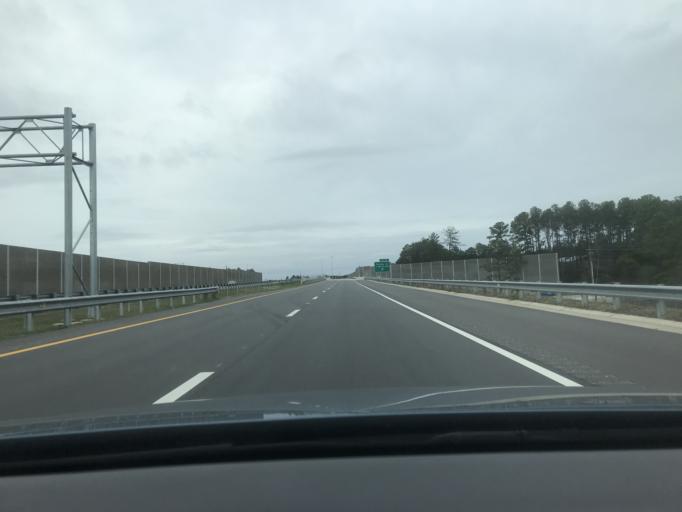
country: US
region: North Carolina
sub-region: Cumberland County
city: Fort Bragg
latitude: 35.1072
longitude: -79.0015
